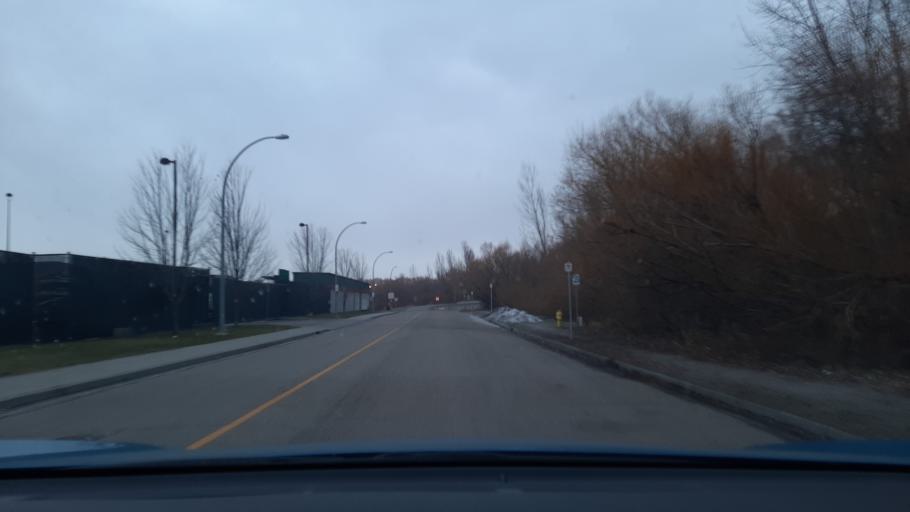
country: CA
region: British Columbia
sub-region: Regional District of North Okanagan
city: Vernon
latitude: 50.2897
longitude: -119.2581
